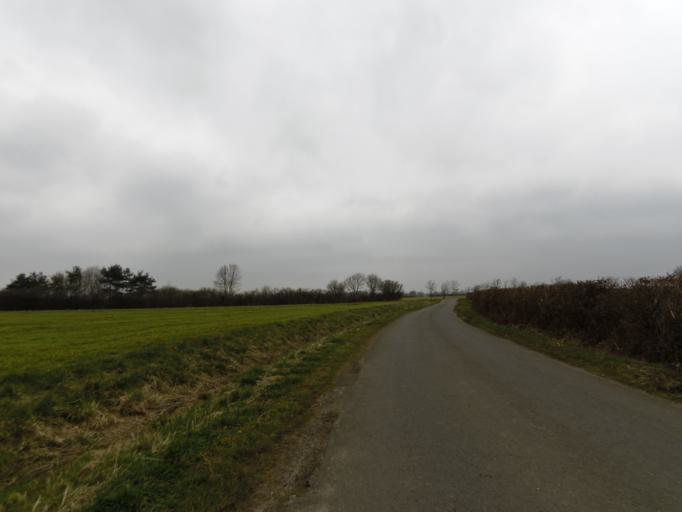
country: GB
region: England
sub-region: Suffolk
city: Framlingham
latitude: 52.2341
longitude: 1.3775
